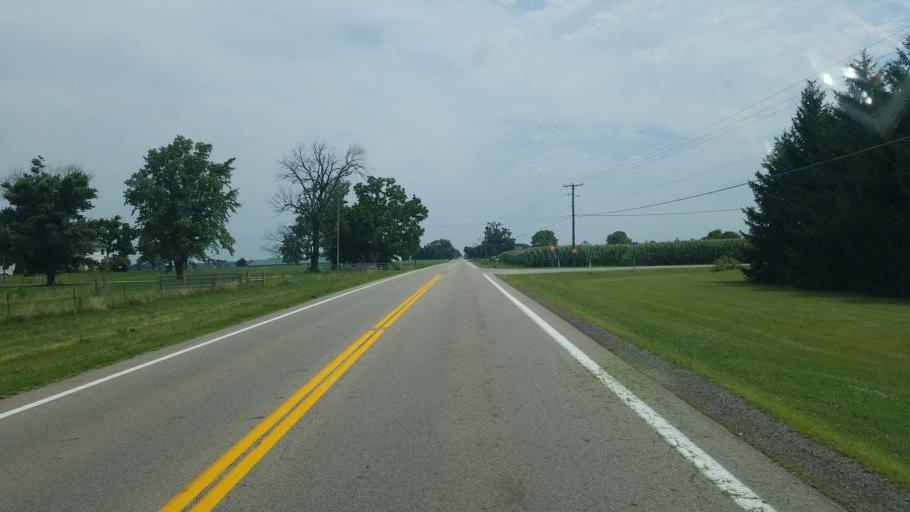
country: US
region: Ohio
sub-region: Madison County
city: West Jefferson
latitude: 39.9750
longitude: -83.3527
